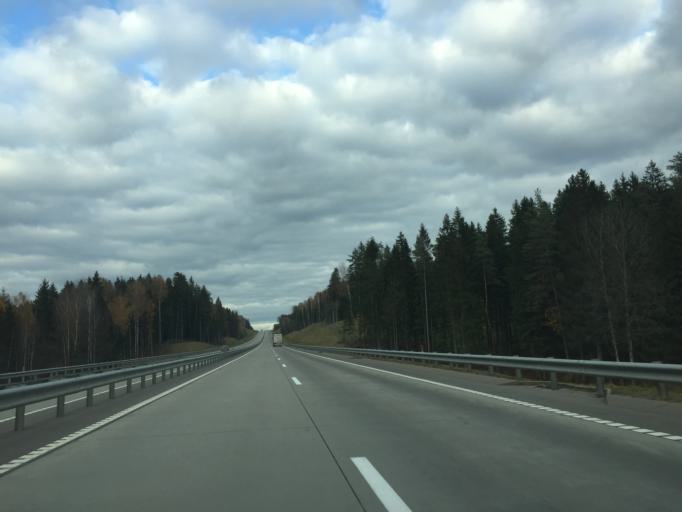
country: BY
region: Minsk
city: Rakaw
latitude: 53.9870
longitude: 27.1066
